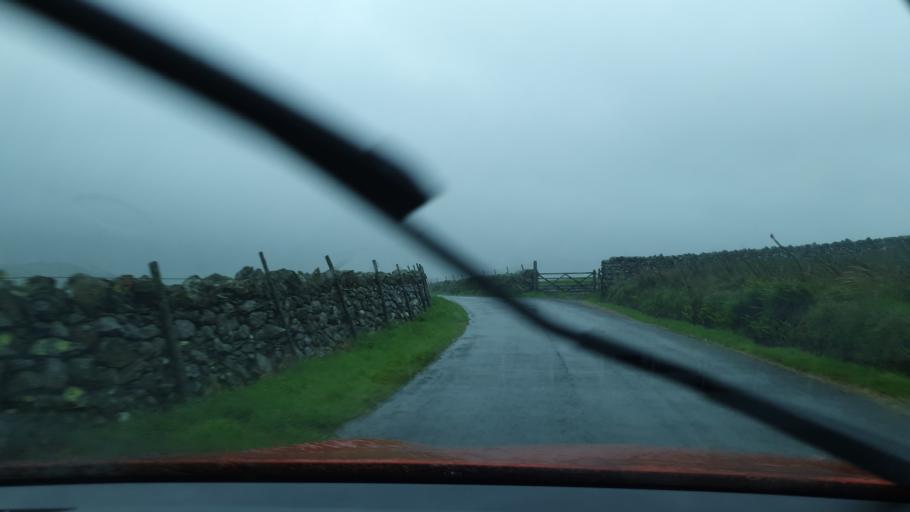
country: GB
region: England
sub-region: Cumbria
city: Millom
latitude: 54.3421
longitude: -3.2478
